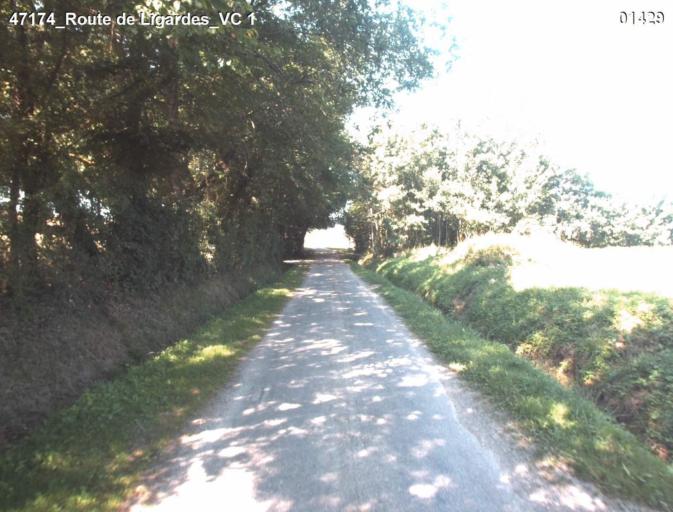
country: FR
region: Midi-Pyrenees
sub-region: Departement du Gers
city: Condom
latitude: 44.0341
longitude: 0.4034
